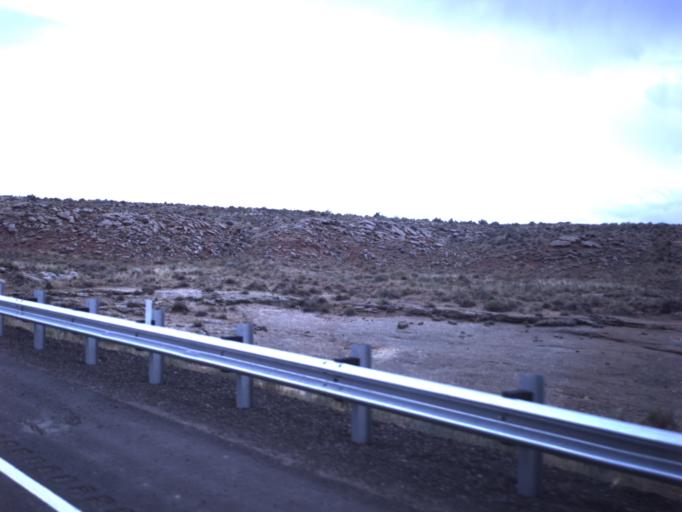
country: US
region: Utah
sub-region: Uintah County
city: Naples
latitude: 40.2632
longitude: -109.4506
